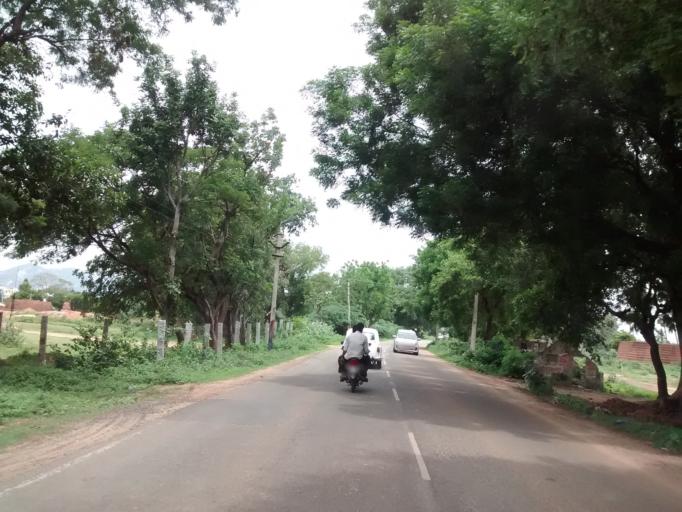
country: IN
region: Andhra Pradesh
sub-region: Chittoor
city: Narasingapuram
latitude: 13.6113
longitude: 79.3544
